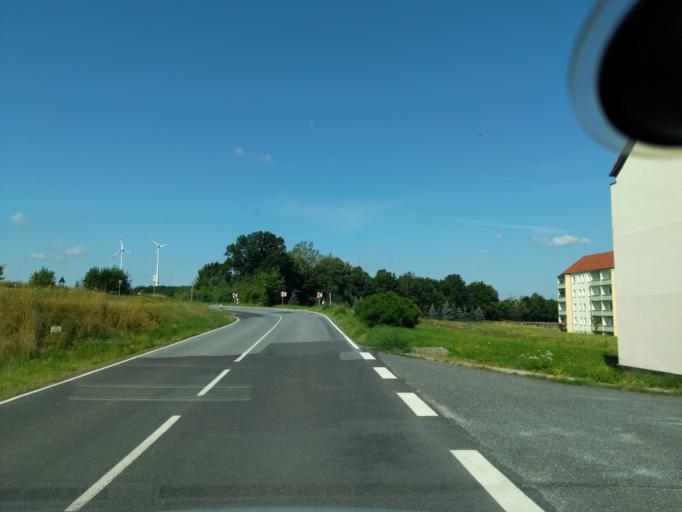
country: DE
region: Saxony
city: Lobau
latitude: 51.1300
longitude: 14.6740
